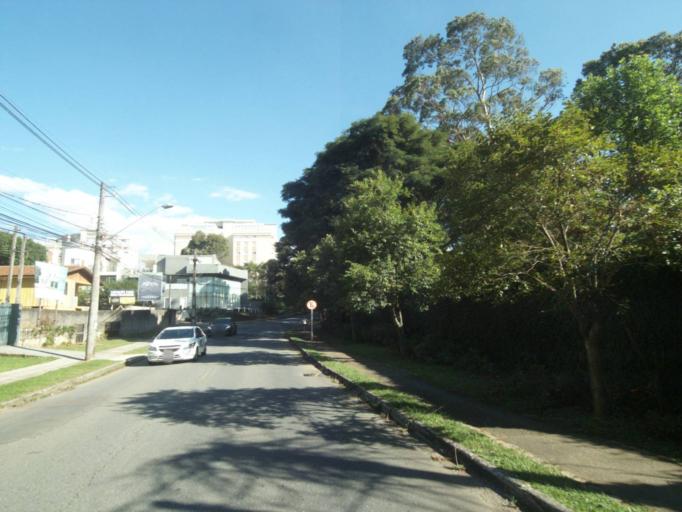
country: BR
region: Parana
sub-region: Curitiba
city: Curitiba
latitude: -25.4436
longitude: -49.3222
